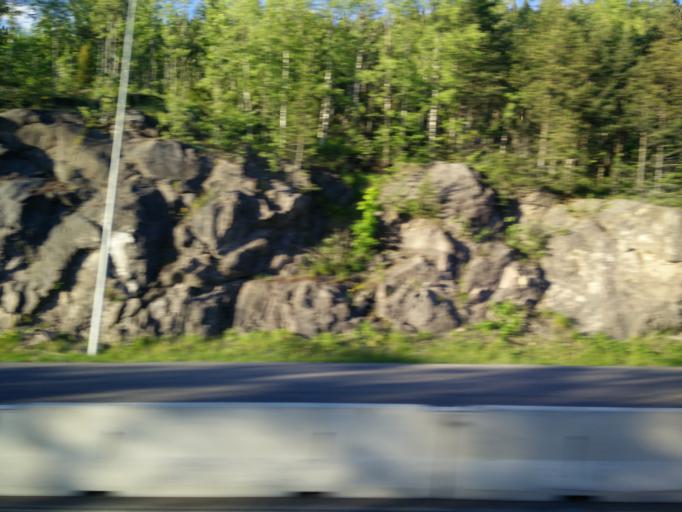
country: NO
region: Buskerud
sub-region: Hole
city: Vik
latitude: 59.9834
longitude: 10.3087
